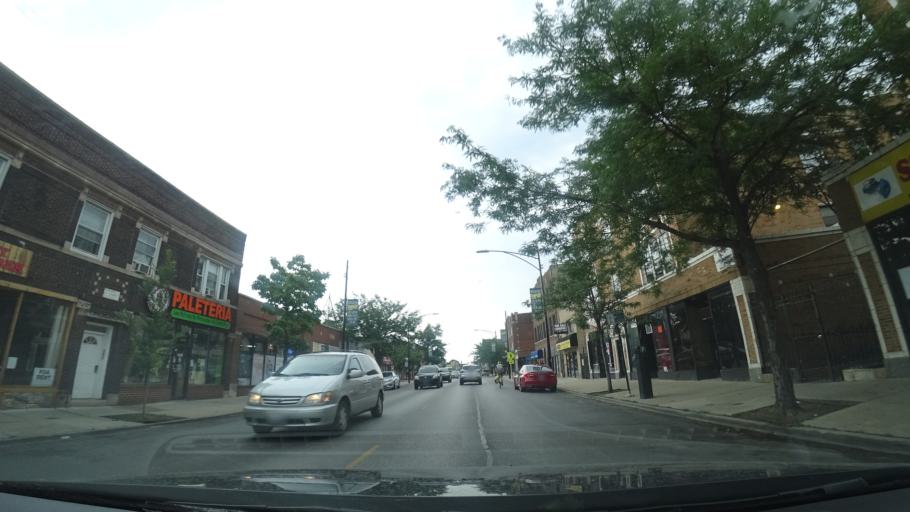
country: US
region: Illinois
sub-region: Cook County
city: Evanston
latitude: 42.0032
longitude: -87.6724
